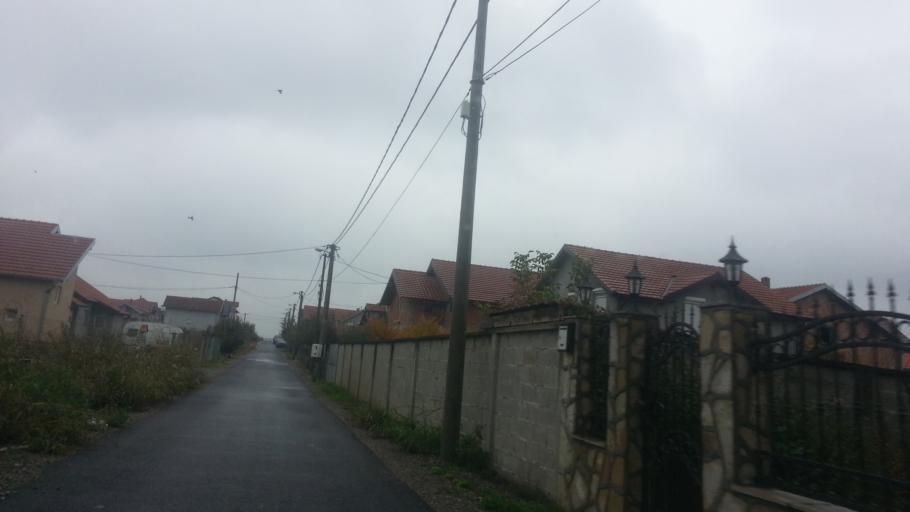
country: RS
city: Novi Banovci
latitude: 44.9076
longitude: 20.2952
